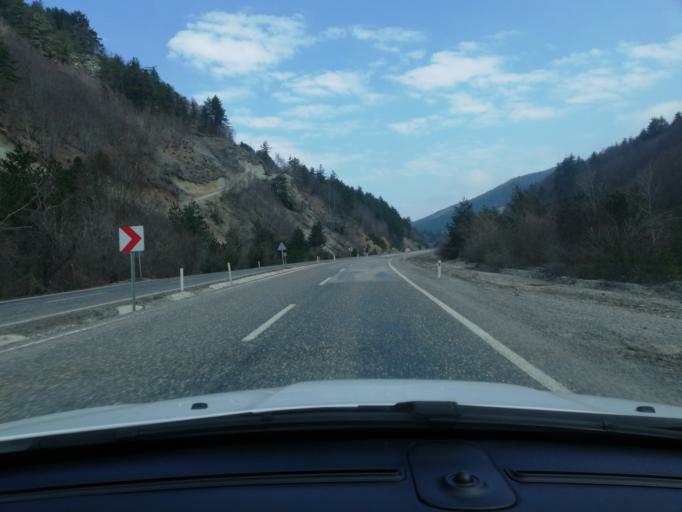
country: TR
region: Kastamonu
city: Kuzyaka
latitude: 41.1689
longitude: 33.7937
